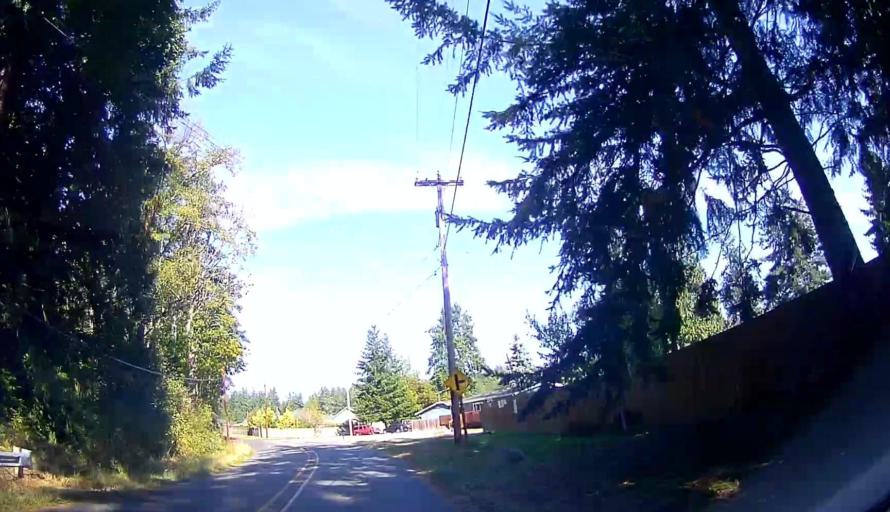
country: US
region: Washington
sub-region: Island County
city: Camano
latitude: 48.1770
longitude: -122.5209
